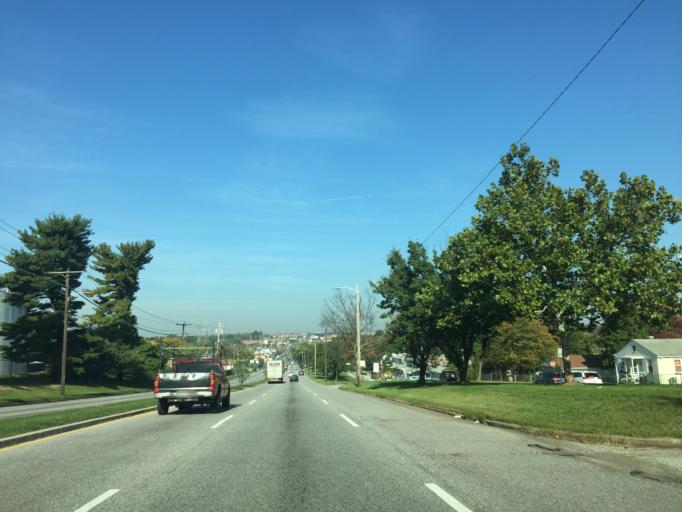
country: US
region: Maryland
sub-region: Baltimore County
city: Rosedale
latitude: 39.3039
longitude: -76.5547
